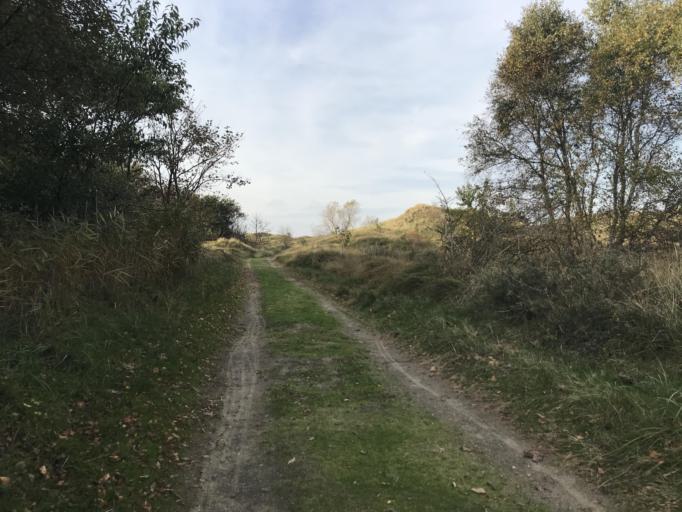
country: DE
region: Lower Saxony
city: Borkum
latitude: 53.6048
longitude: 6.7636
